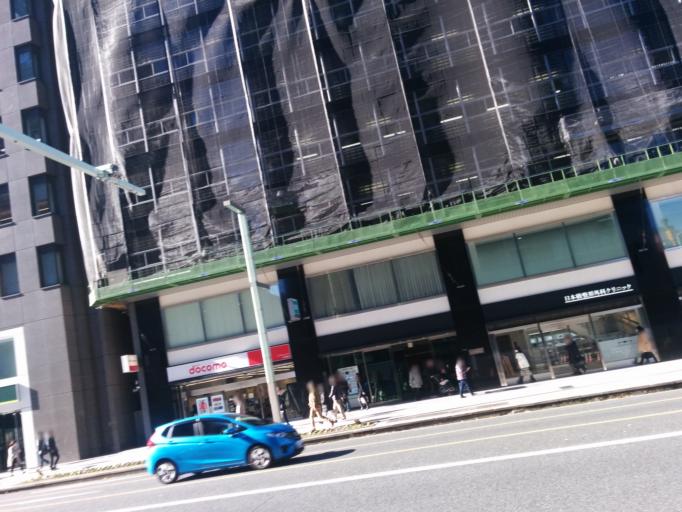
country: JP
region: Tokyo
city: Tokyo
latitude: 35.6823
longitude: 139.7737
